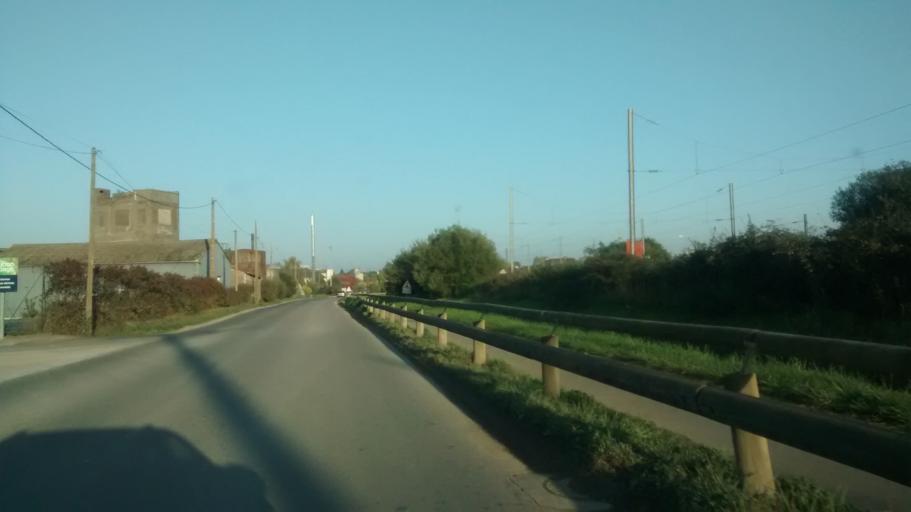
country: FR
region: Brittany
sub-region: Departement d'Ille-et-Vilaine
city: Saint-Gilles
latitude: 48.1225
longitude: -1.8260
